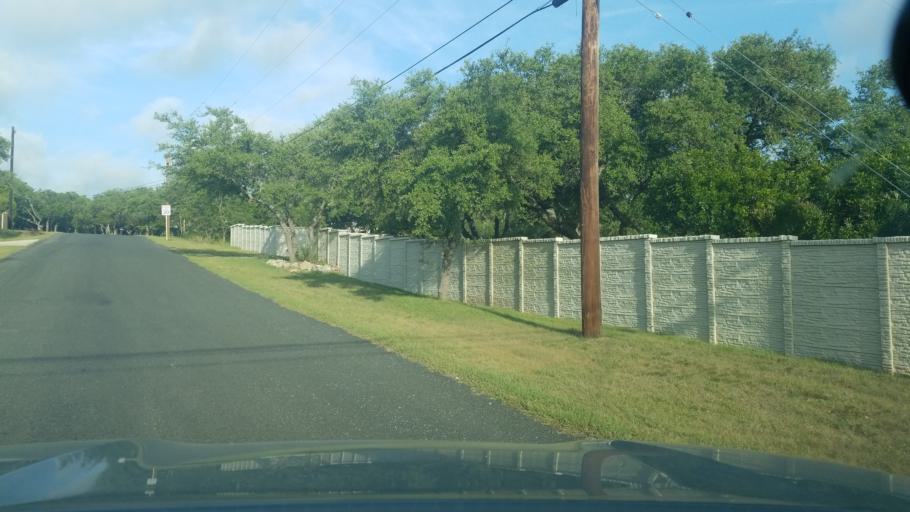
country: US
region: Texas
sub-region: Bexar County
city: Timberwood Park
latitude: 29.7056
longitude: -98.5175
